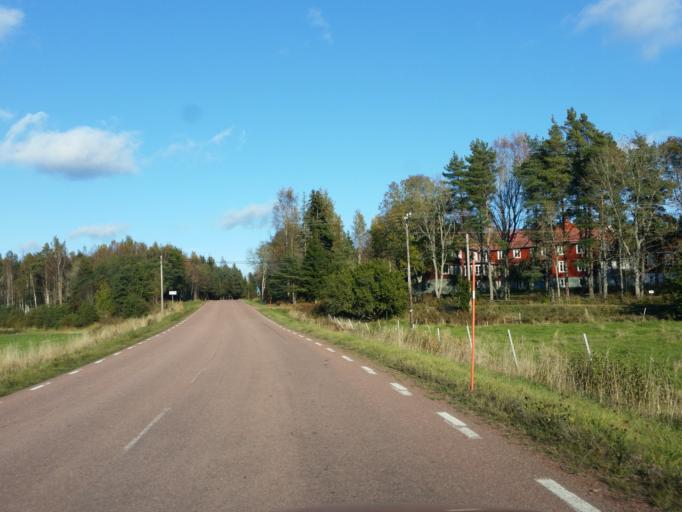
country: AX
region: Alands landsbygd
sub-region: Jomala
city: Jomala
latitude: 60.1553
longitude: 19.8750
